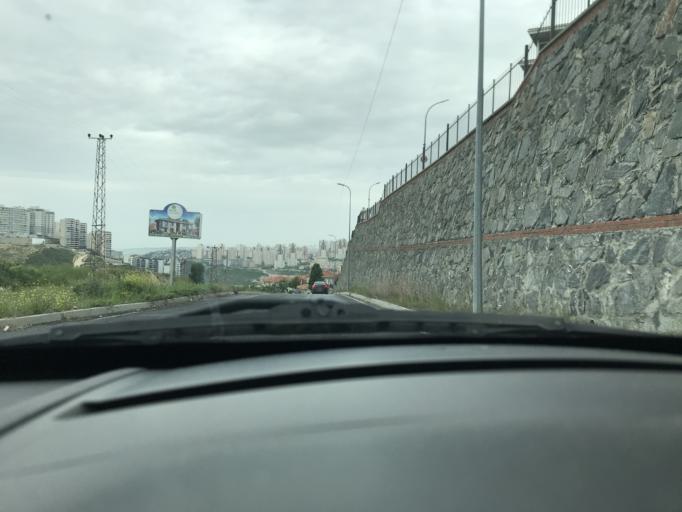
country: TR
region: Istanbul
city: Esenyurt
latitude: 41.0917
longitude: 28.6817
